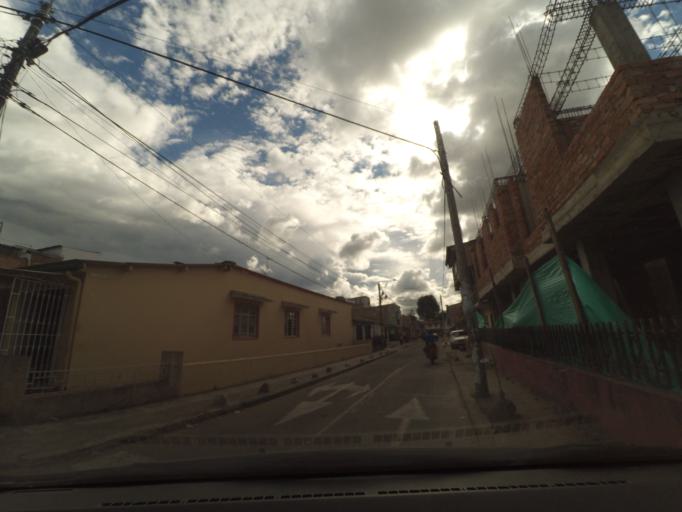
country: CO
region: Cauca
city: Popayan
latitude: 2.4418
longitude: -76.6163
